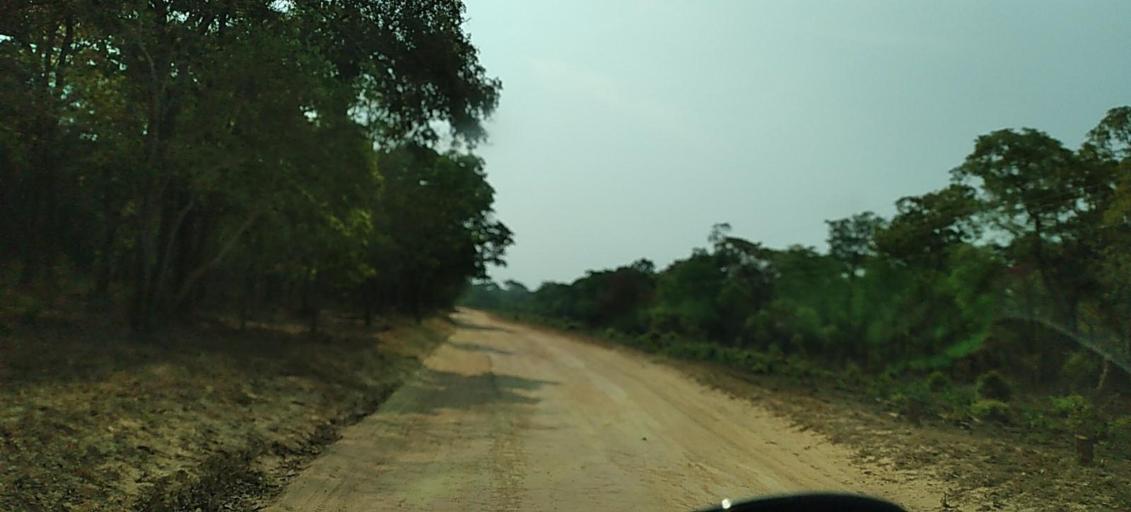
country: ZM
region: North-Western
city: Solwezi
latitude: -12.6831
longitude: 26.3883
